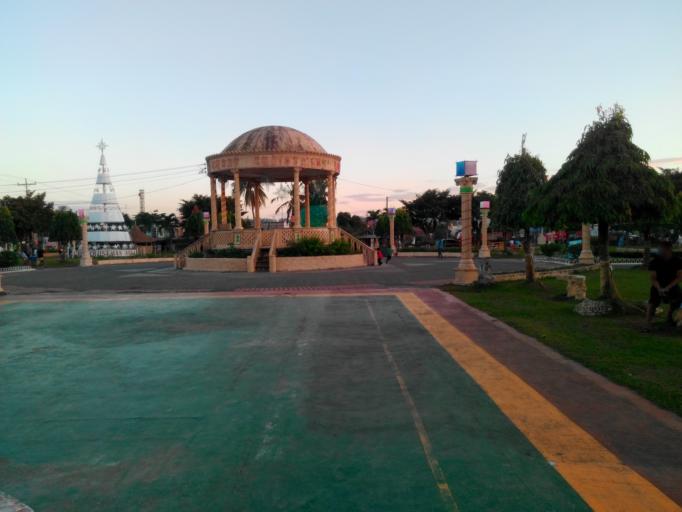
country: PH
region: Western Visayas
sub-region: Province of Iloilo
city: Passi
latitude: 11.1054
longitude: 122.6415
